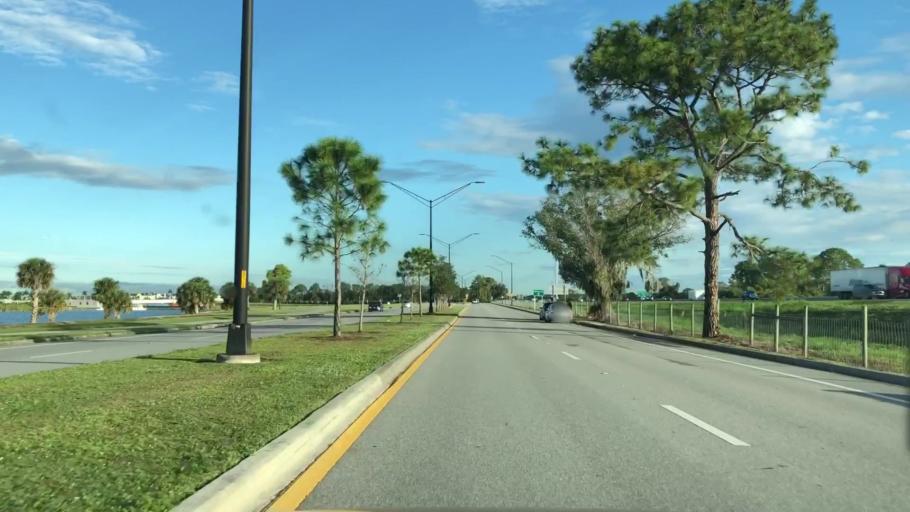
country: US
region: Florida
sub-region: Sarasota County
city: The Meadows
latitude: 27.3690
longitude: -82.4473
